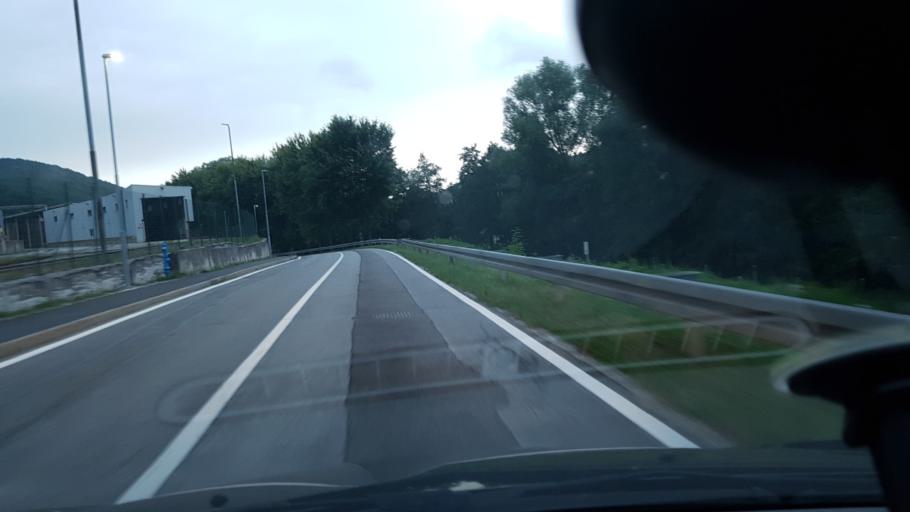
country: SI
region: Rogatec
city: Rogatec
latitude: 46.2231
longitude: 15.7103
